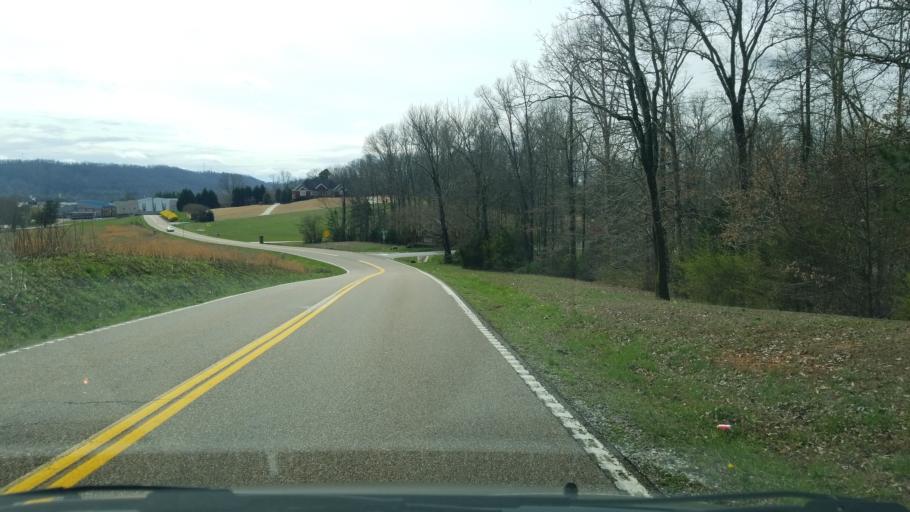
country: US
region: Tennessee
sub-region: Hamilton County
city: Collegedale
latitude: 35.0989
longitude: -85.0646
